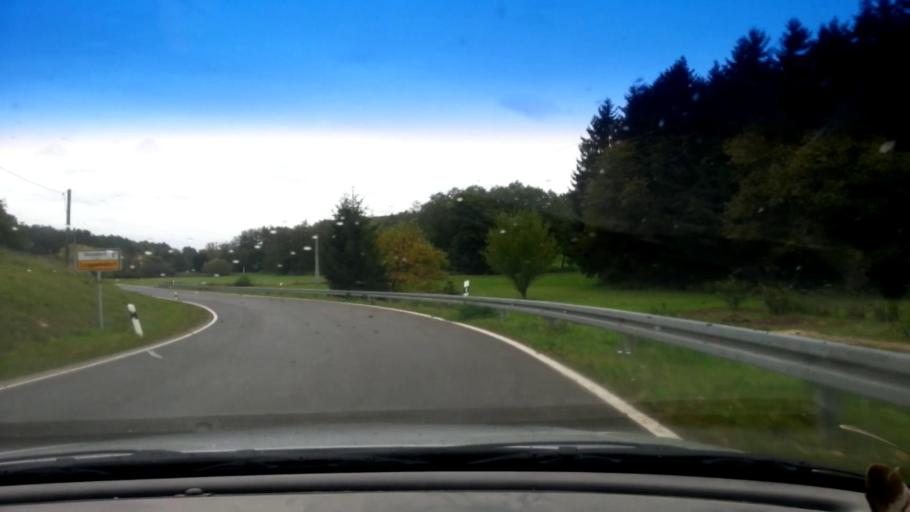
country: DE
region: Bavaria
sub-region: Upper Franconia
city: Lauter
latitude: 49.9888
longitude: 10.7592
